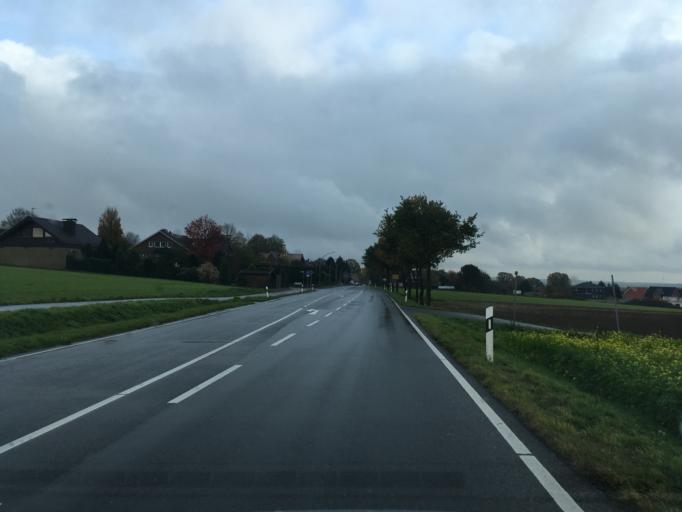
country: DE
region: North Rhine-Westphalia
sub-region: Regierungsbezirk Munster
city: Klein Reken
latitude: 51.8365
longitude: 7.0350
